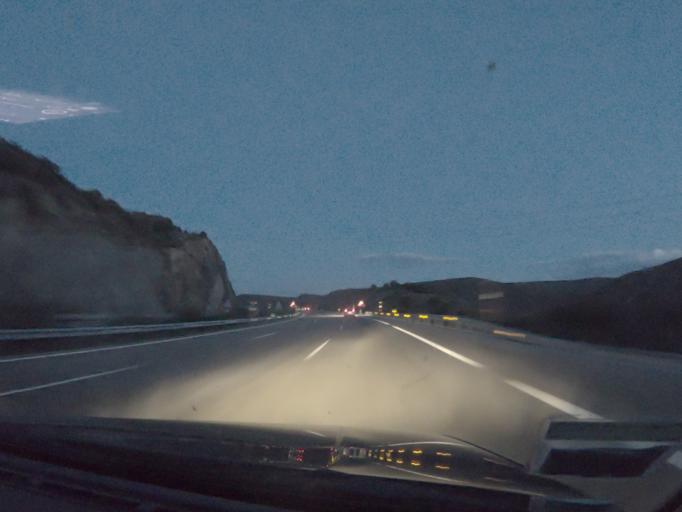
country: ES
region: Castille and Leon
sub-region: Provincia de Leon
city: Folgoso de la Ribera
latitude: 42.6056
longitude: -6.2659
